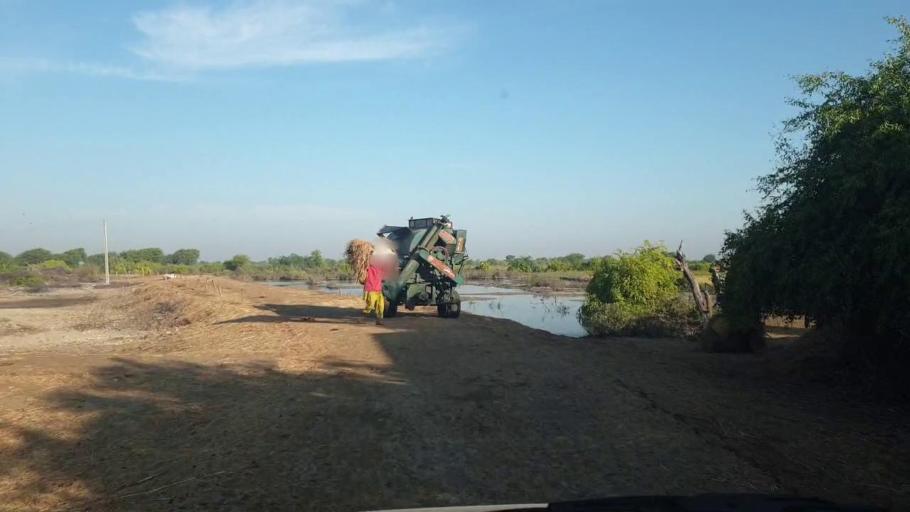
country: PK
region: Sindh
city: Talhar
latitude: 24.8089
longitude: 68.8533
